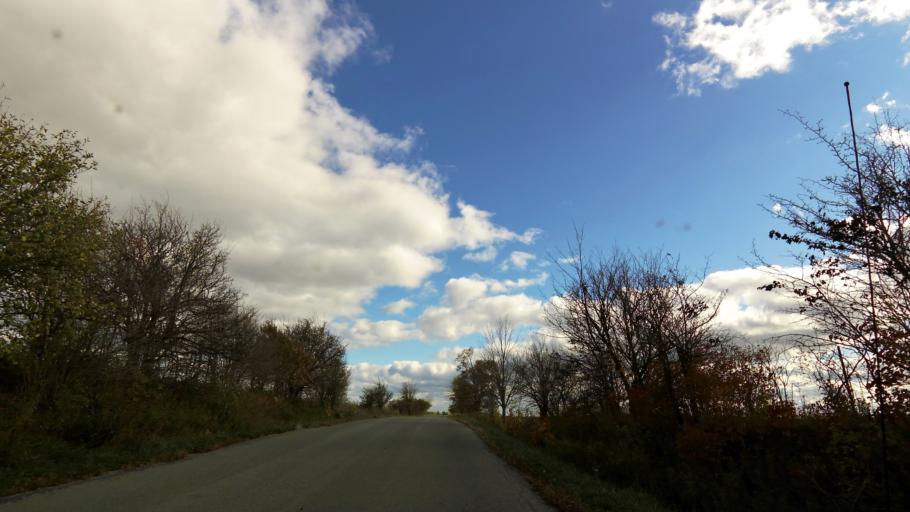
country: CA
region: Ontario
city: Burlington
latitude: 43.4388
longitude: -79.8377
